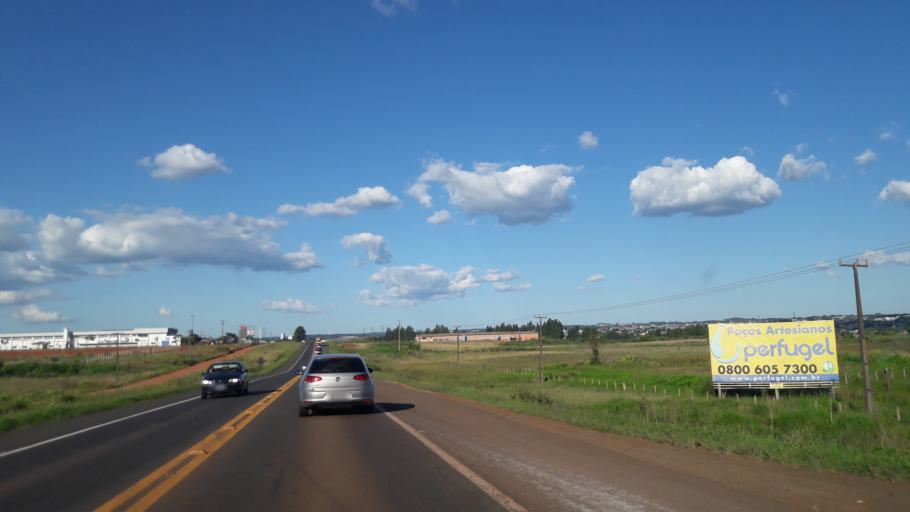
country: BR
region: Parana
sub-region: Guarapuava
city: Guarapuava
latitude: -25.3849
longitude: -51.5136
